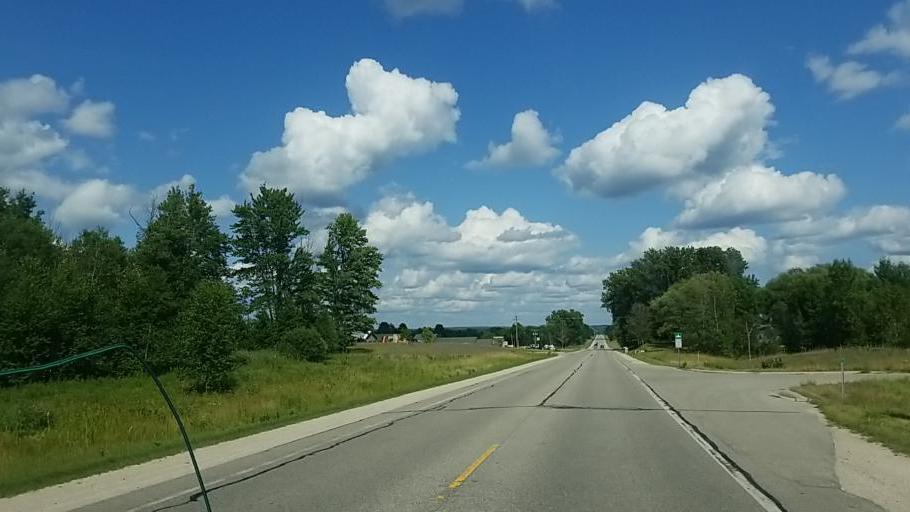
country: US
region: Michigan
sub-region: Osceola County
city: Reed City
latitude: 43.8876
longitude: -85.5609
